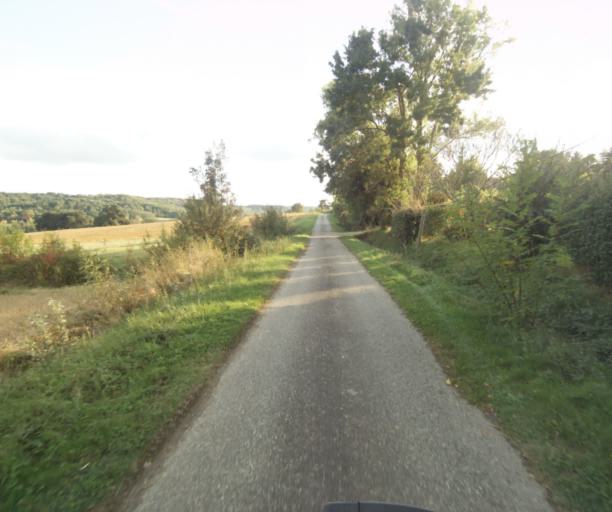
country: FR
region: Midi-Pyrenees
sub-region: Departement de la Haute-Garonne
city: Launac
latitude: 43.8219
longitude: 1.1232
